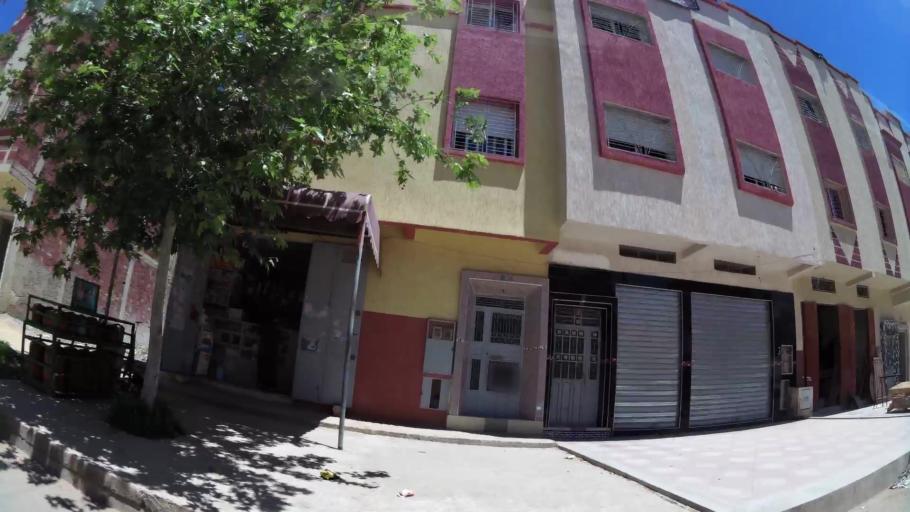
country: MA
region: Meknes-Tafilalet
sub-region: Meknes
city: Meknes
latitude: 33.8640
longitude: -5.5626
